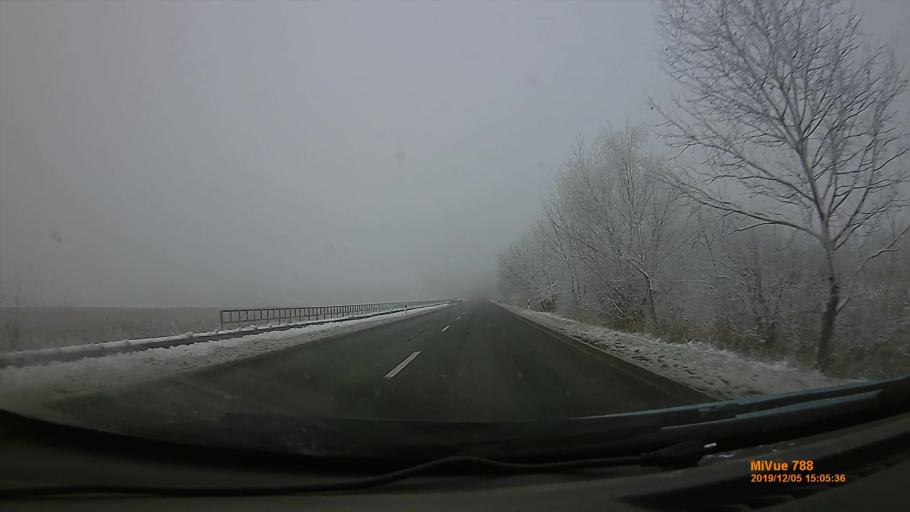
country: HU
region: Szabolcs-Szatmar-Bereg
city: Tiszanagyfalu
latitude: 48.1119
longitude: 21.4851
